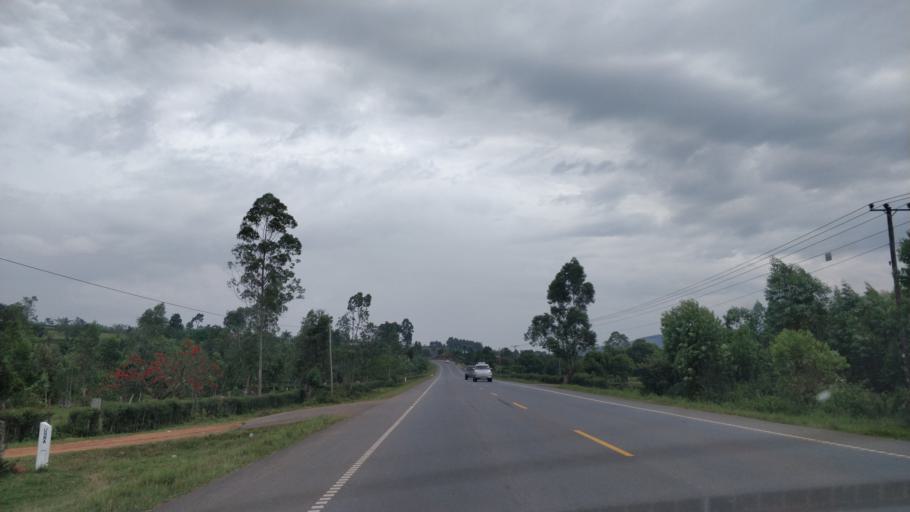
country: UG
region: Western Region
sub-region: Sheema District
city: Kibingo
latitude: -0.6563
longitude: 30.4770
